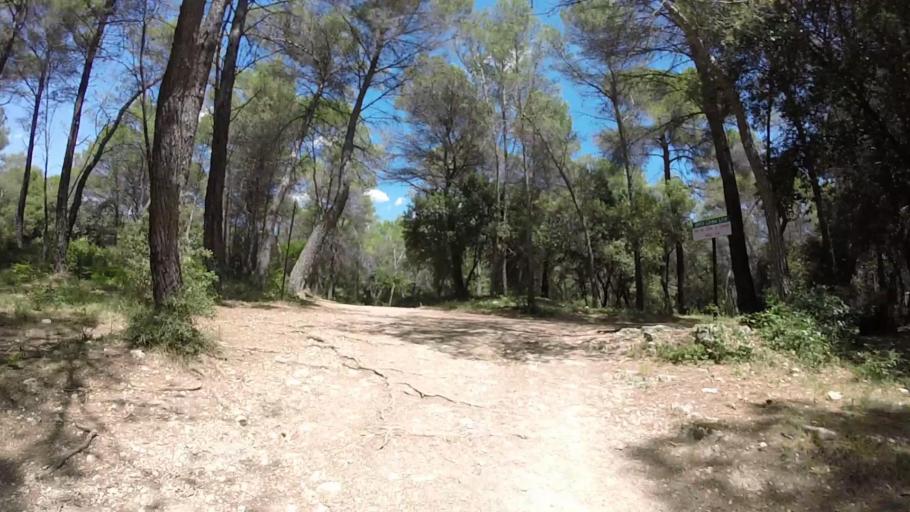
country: FR
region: Provence-Alpes-Cote d'Azur
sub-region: Departement des Alpes-Maritimes
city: Mougins
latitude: 43.5976
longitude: 7.0228
